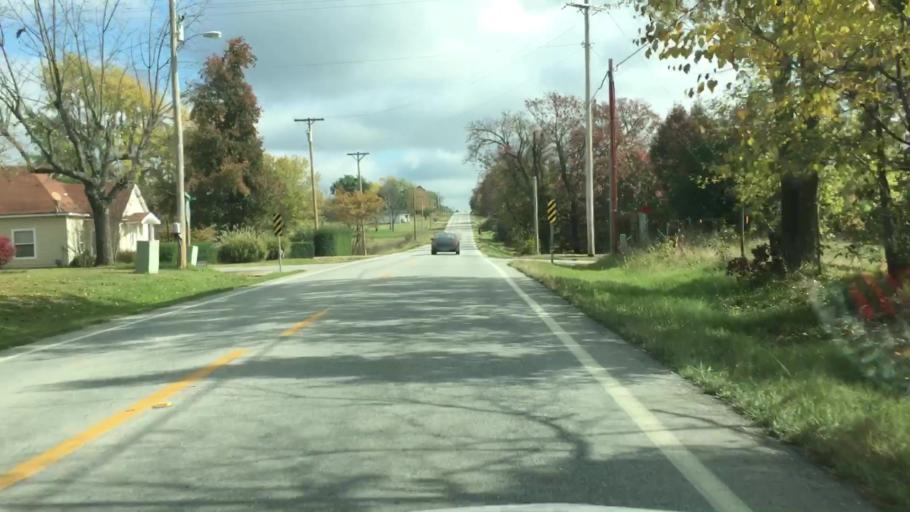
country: US
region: Arkansas
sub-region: Benton County
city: Gentry
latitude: 36.2638
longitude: -94.4720
